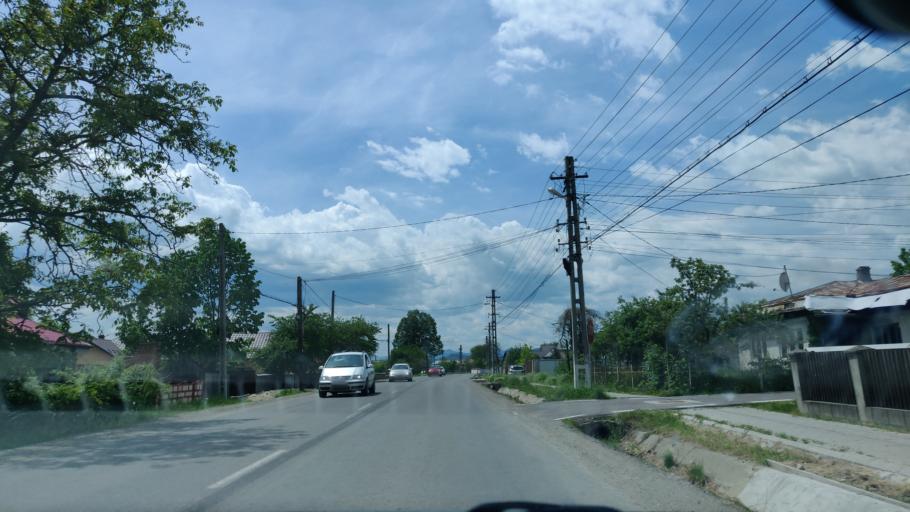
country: RO
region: Vrancea
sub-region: Comuna Vidra
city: Vidra
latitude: 45.9086
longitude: 26.9011
